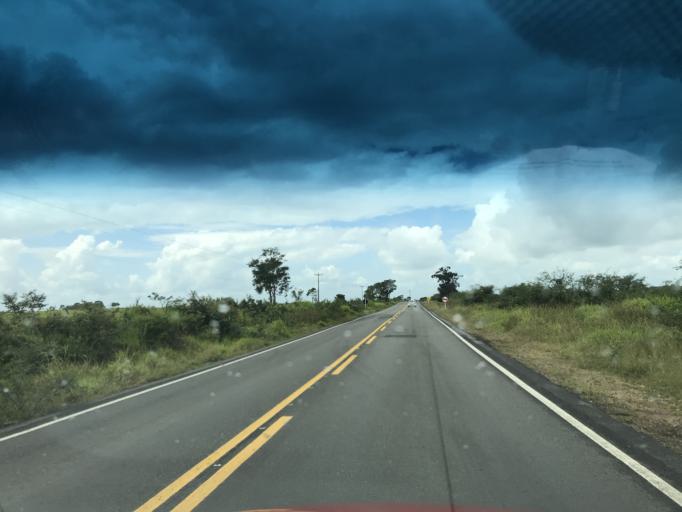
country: BR
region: Bahia
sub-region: Conceicao Do Almeida
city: Conceicao do Almeida
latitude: -12.6762
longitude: -39.2634
